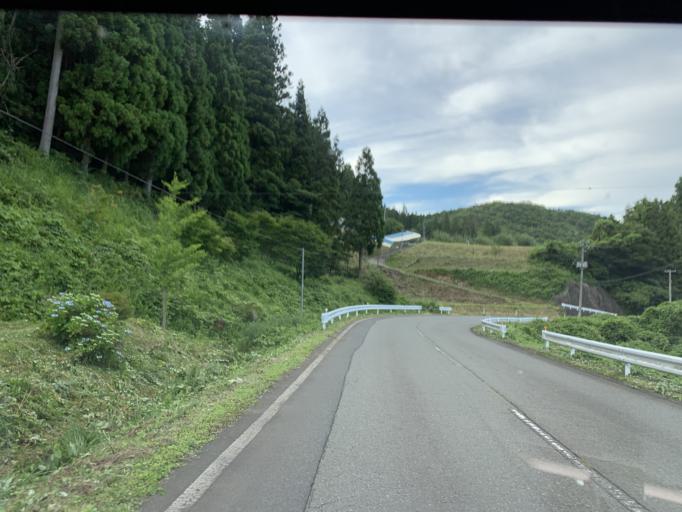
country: JP
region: Iwate
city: Ichinoseki
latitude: 38.8960
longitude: 141.0088
